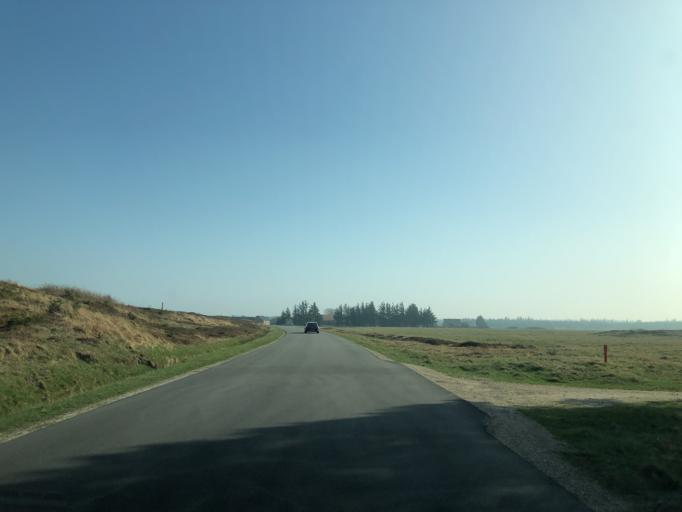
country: DK
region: South Denmark
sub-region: Varde Kommune
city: Oksbol
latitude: 55.6452
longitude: 8.1779
